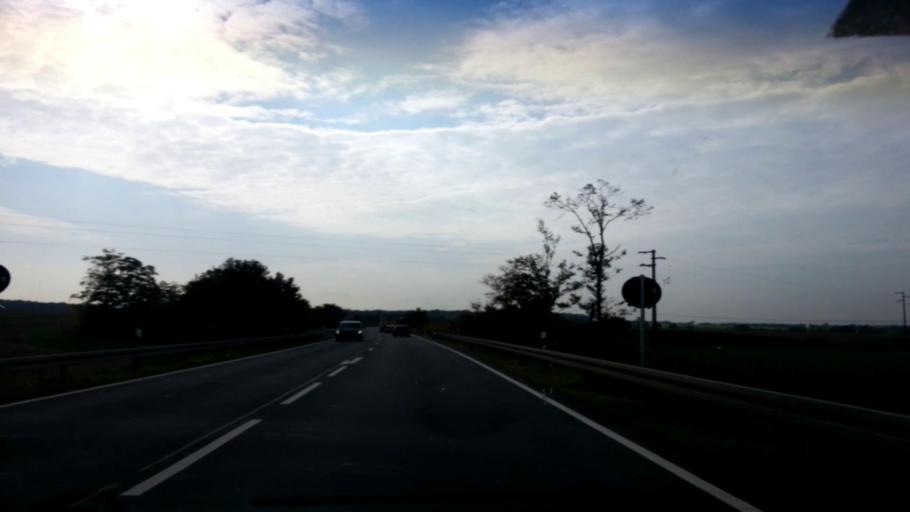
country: DE
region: Bavaria
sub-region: Regierungsbezirk Unterfranken
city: Prichsenstadt
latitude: 49.8432
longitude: 10.3511
